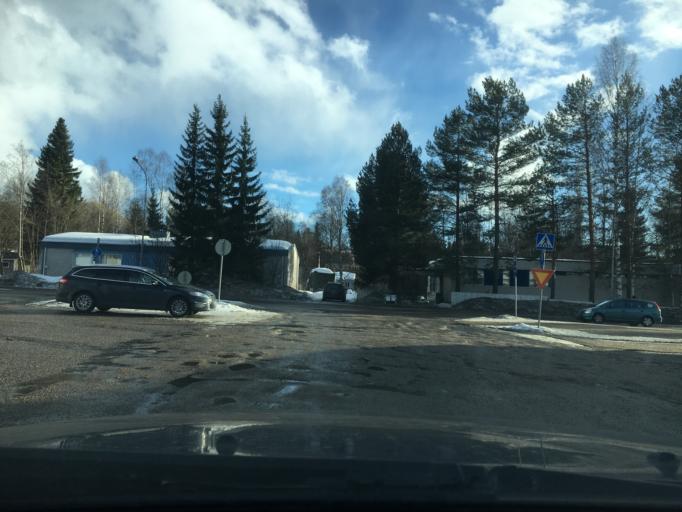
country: FI
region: Kainuu
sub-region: Kajaani
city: Kajaani
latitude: 64.2181
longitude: 27.7434
